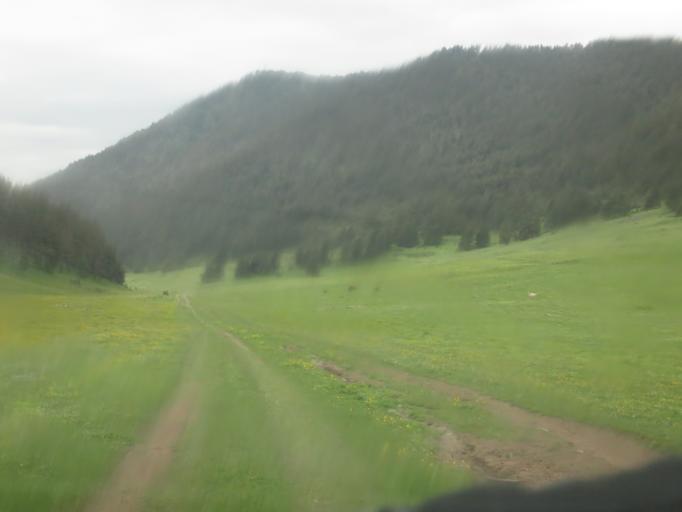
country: RU
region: Chechnya
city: Itum-Kali
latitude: 42.3934
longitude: 45.6839
